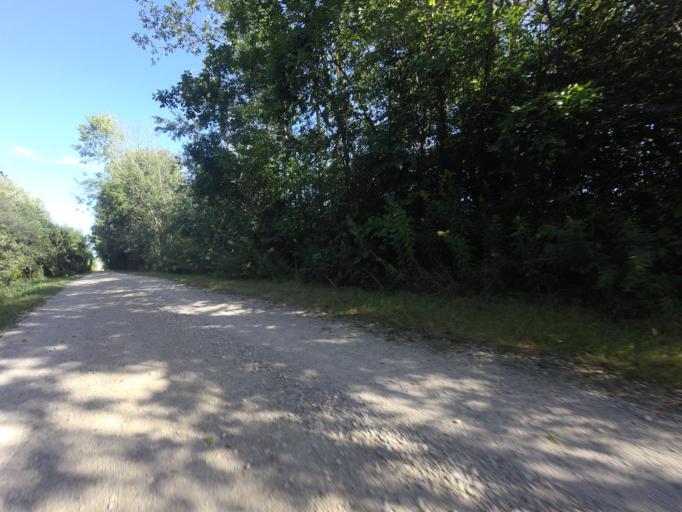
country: CA
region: Ontario
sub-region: Wellington County
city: Guelph
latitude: 43.6637
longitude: -80.4337
